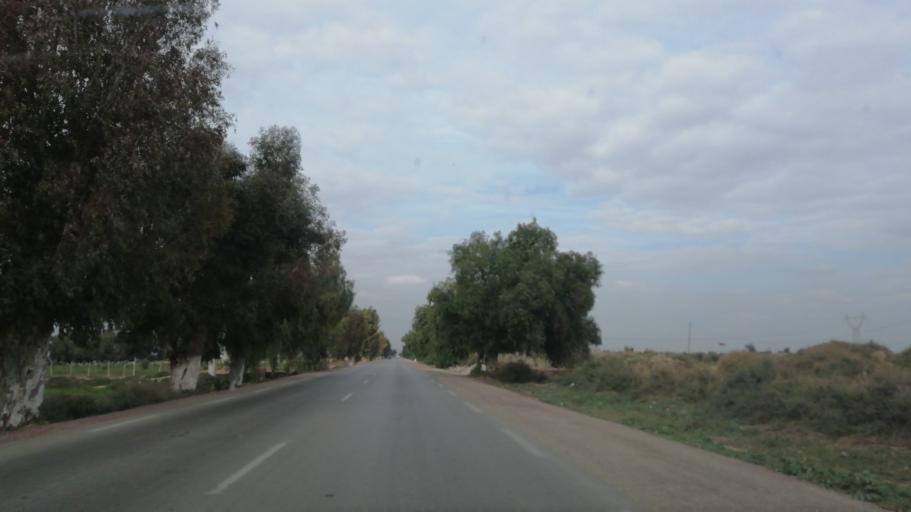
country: DZ
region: Mascara
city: Mascara
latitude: 35.6349
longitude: 0.0609
